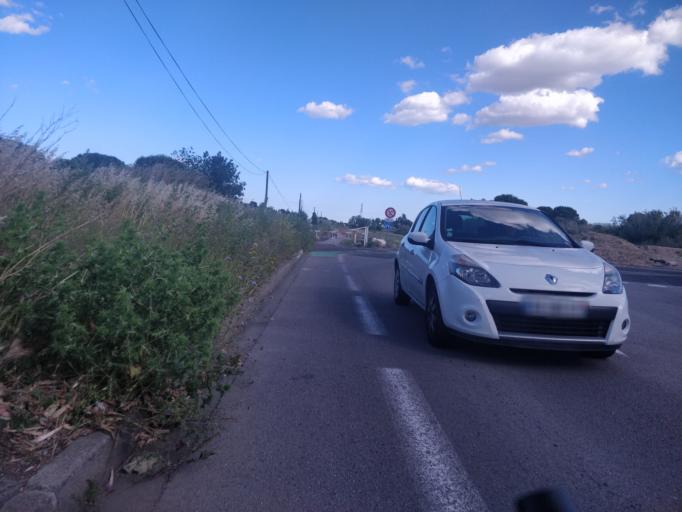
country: FR
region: Languedoc-Roussillon
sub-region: Departement des Pyrenees-Orientales
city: Perpignan
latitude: 42.6823
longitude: 2.9152
